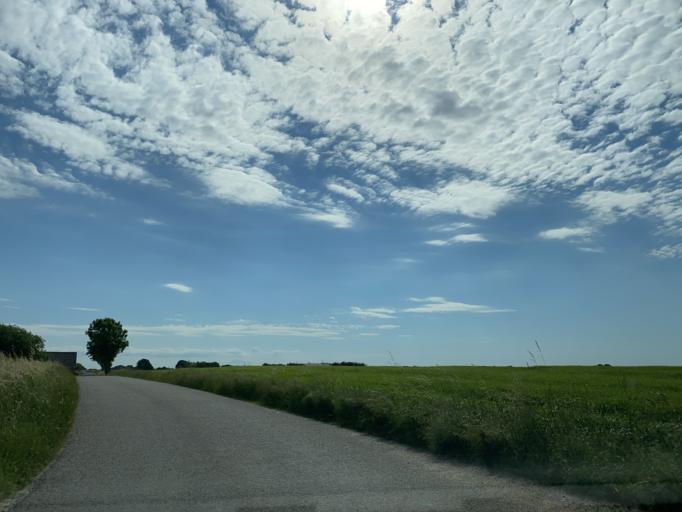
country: DK
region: Central Jutland
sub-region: Favrskov Kommune
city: Hammel
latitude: 56.2140
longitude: 9.8892
